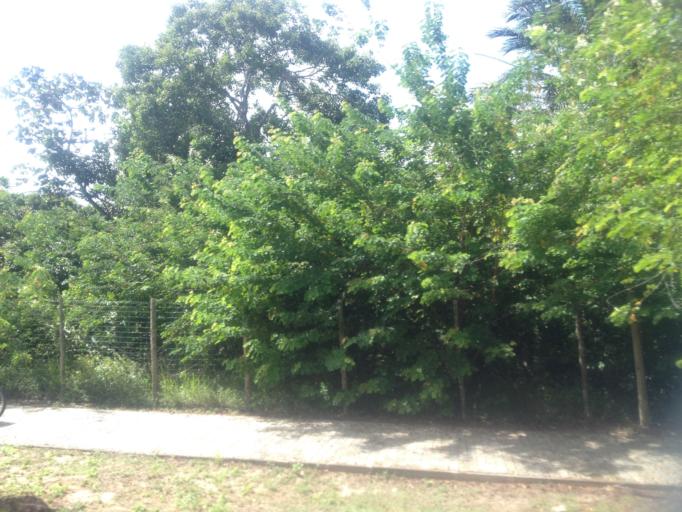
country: BR
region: Bahia
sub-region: Mata De Sao Joao
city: Mata de Sao Joao
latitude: -12.5665
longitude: -38.0172
